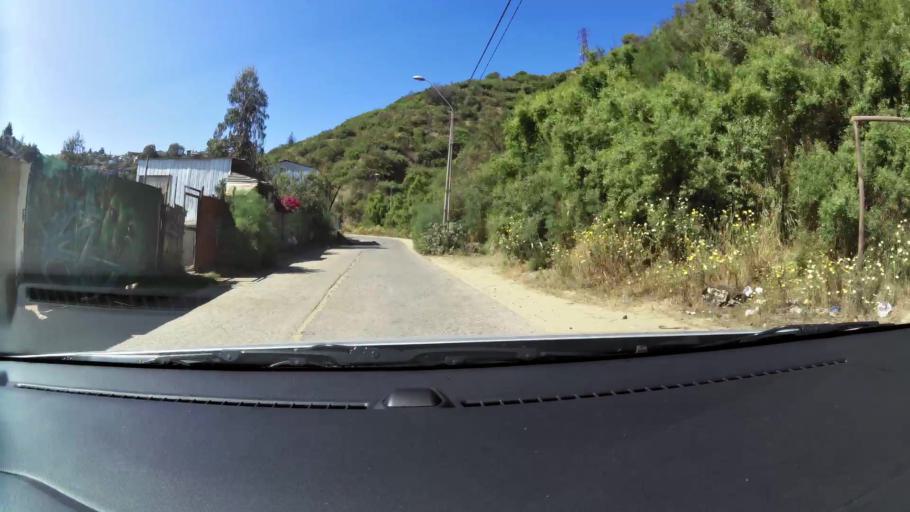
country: CL
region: Valparaiso
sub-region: Provincia de Valparaiso
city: Valparaiso
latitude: -33.0705
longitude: -71.5879
